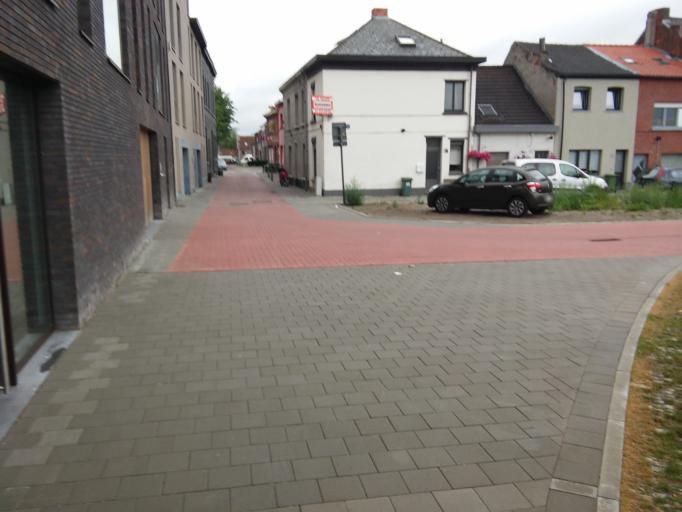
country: BE
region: Flanders
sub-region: Provincie Antwerpen
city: Niel
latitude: 51.0996
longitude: 4.3343
